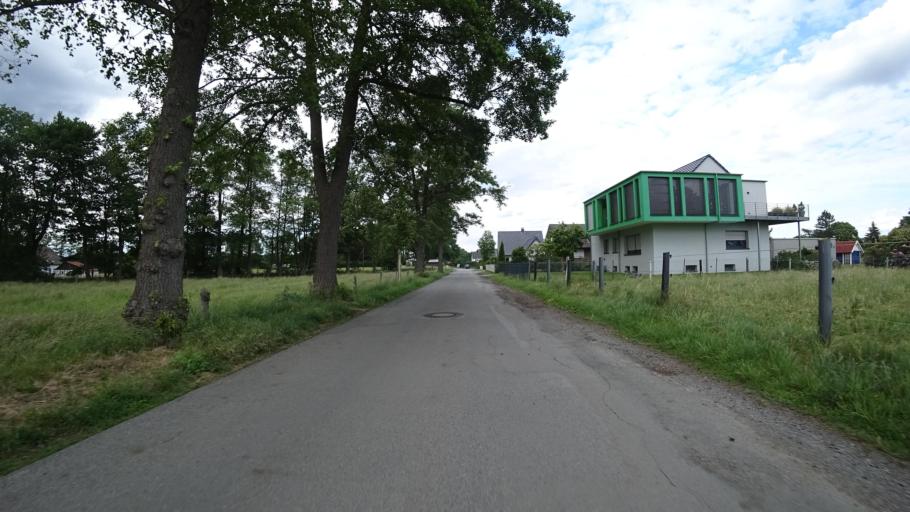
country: DE
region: North Rhine-Westphalia
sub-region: Regierungsbezirk Detmold
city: Guetersloh
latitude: 51.8937
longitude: 8.4322
